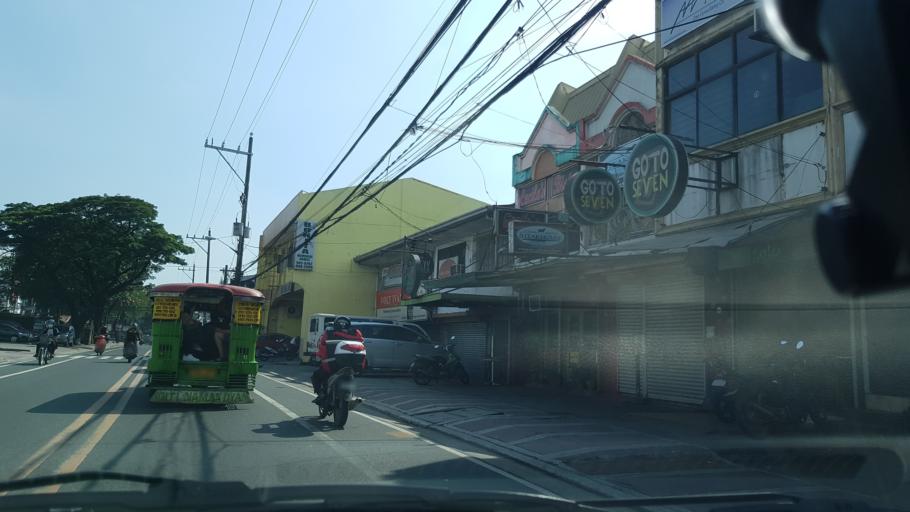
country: PH
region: Metro Manila
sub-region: Marikina
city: Calumpang
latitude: 14.6476
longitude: 121.0969
